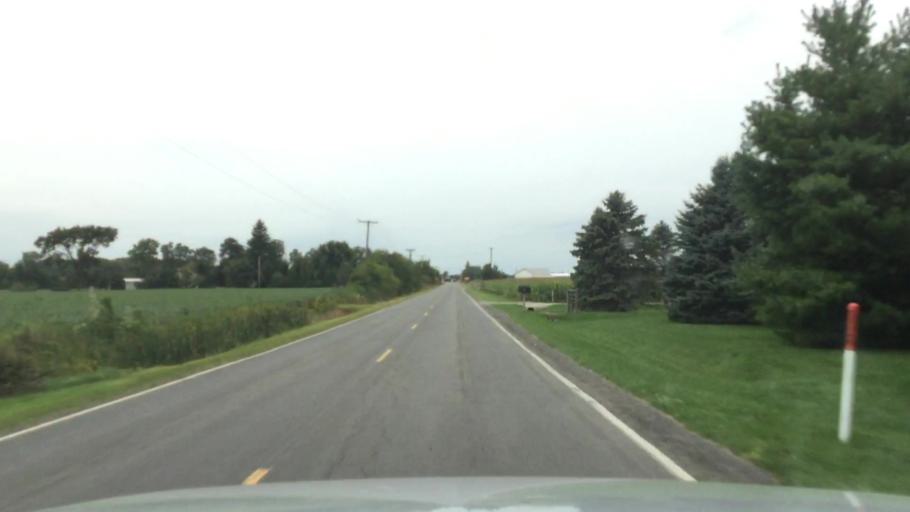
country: US
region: Michigan
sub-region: Washtenaw County
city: Milan
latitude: 42.1131
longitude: -83.6886
